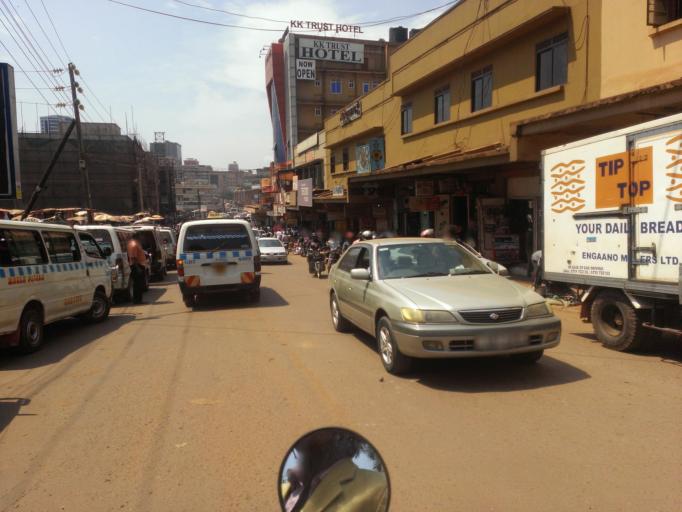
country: UG
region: Central Region
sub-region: Kampala District
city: Kampala
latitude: 0.3133
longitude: 32.5721
